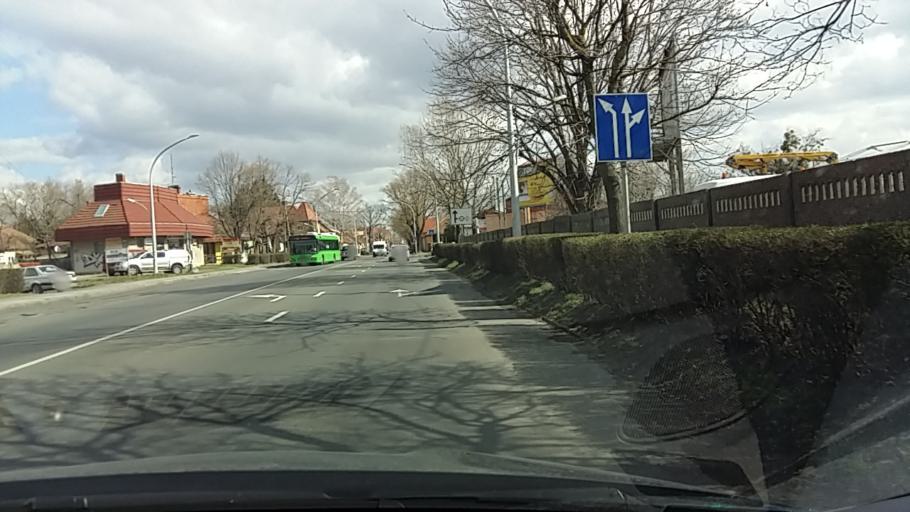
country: HU
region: Baranya
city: Pecs
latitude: 46.0645
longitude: 18.2122
